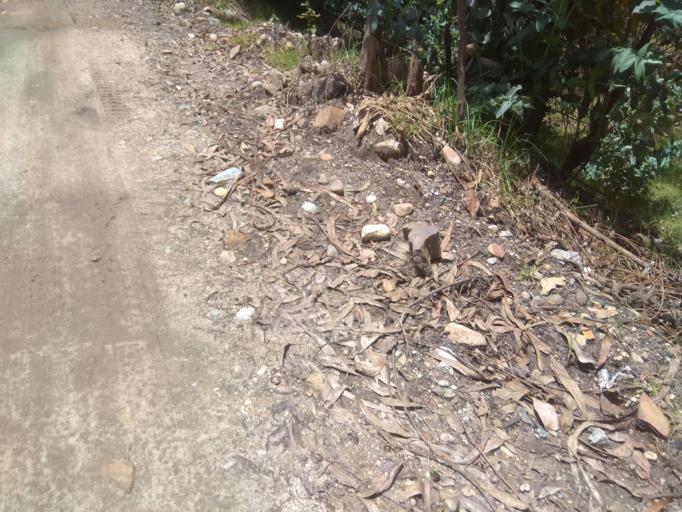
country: CO
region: Boyaca
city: Socha Viejo
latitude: 5.9706
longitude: -72.7384
